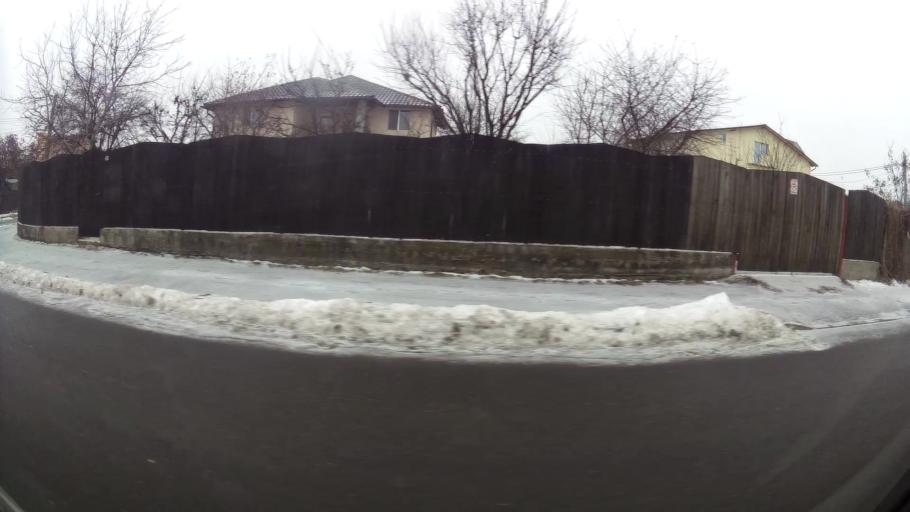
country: RO
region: Prahova
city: Ploiesti
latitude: 44.9544
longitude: 26.0421
